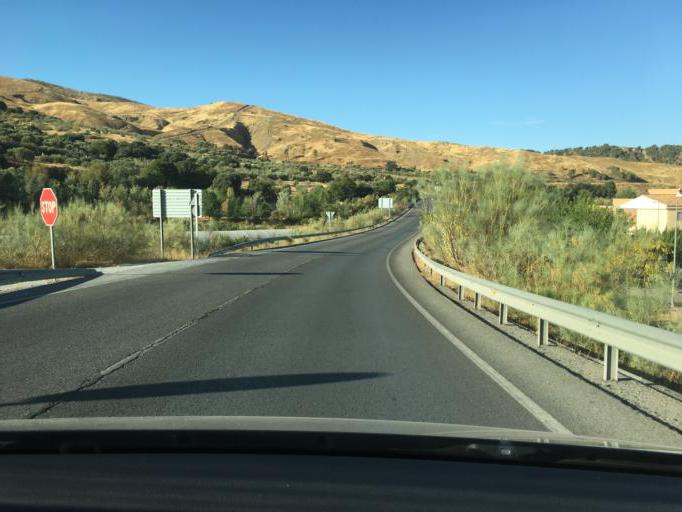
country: ES
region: Andalusia
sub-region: Provincia de Granada
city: Cenes de la Vega
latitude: 37.1565
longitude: -3.5305
